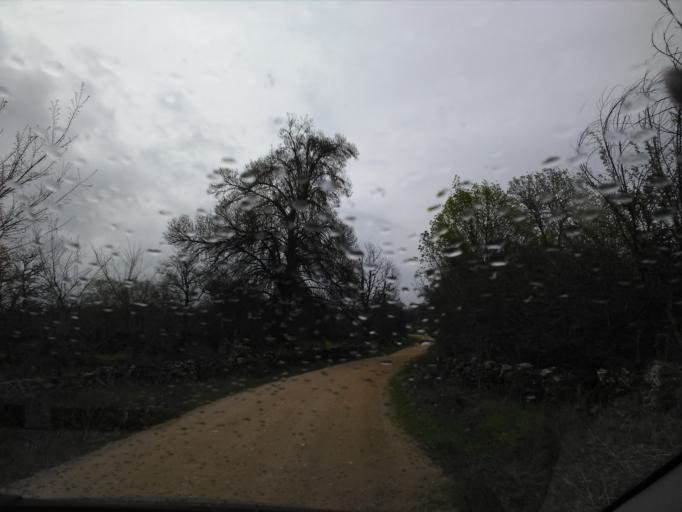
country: ES
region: Castille and Leon
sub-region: Provincia de Salamanca
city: San Felices de los Gallegos
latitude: 40.8437
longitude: -6.7235
